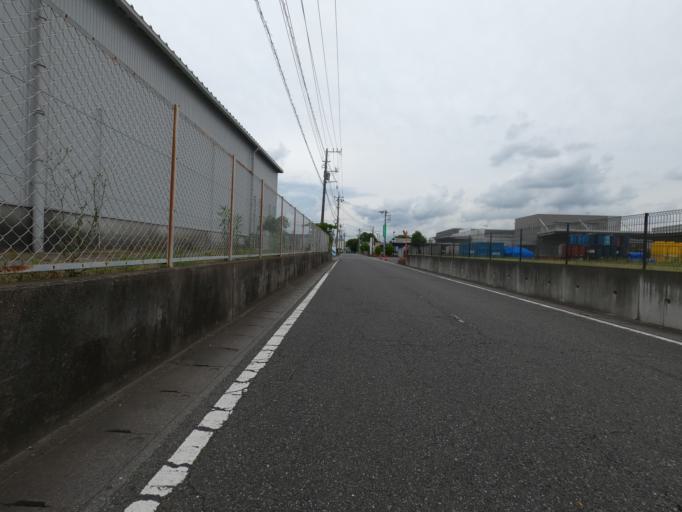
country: JP
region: Ibaraki
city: Moriya
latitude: 35.9567
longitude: 139.9838
